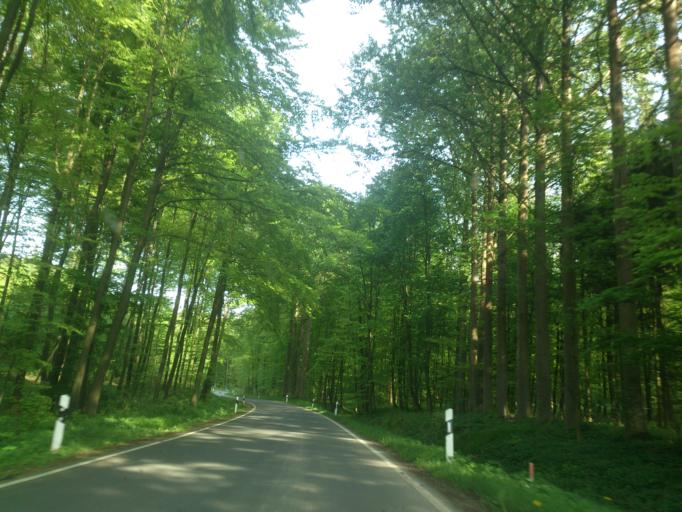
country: DE
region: North Rhine-Westphalia
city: Lichtenau
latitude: 51.6900
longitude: 8.8921
